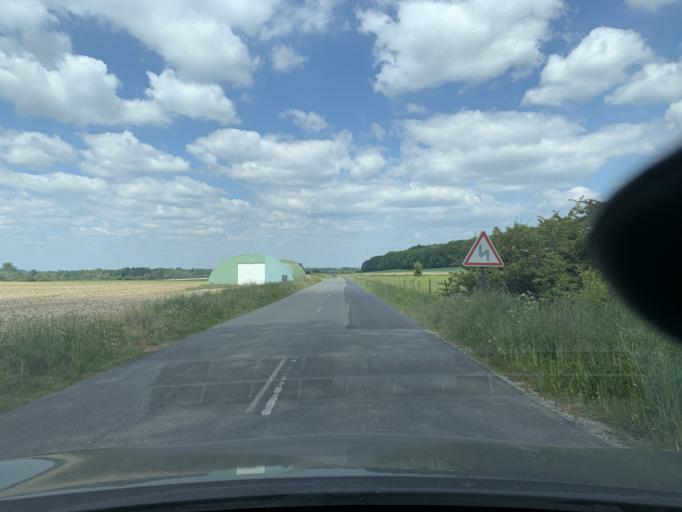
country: FR
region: Nord-Pas-de-Calais
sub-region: Departement du Pas-de-Calais
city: Oisy-le-Verger
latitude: 50.2539
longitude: 3.1146
